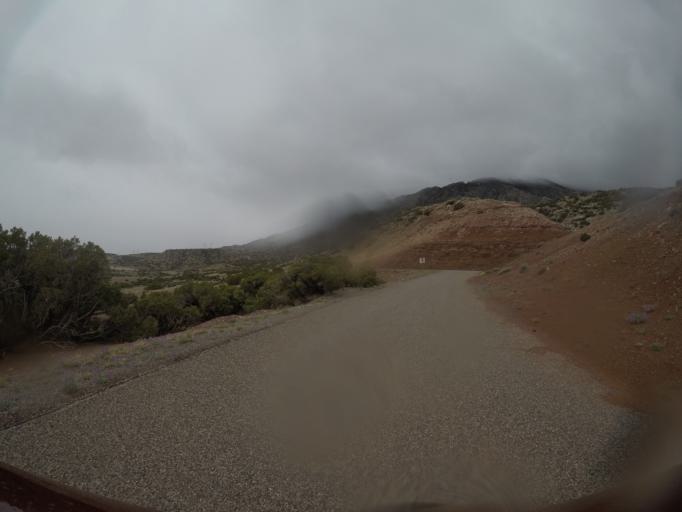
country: US
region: Wyoming
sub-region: Big Horn County
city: Lovell
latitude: 45.0359
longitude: -108.2571
